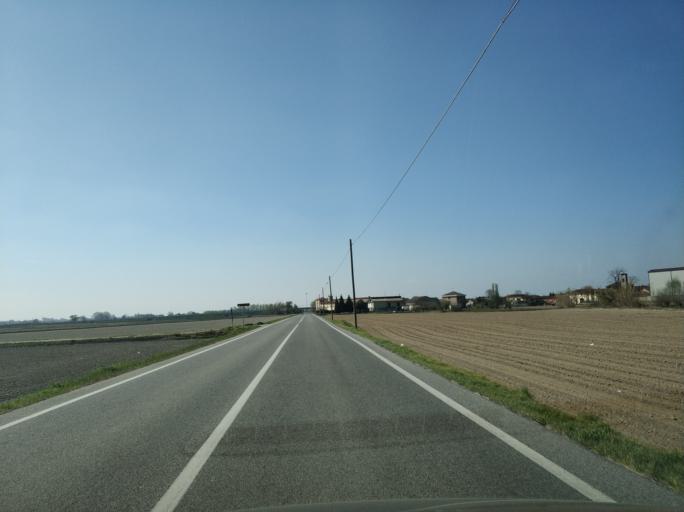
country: IT
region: Piedmont
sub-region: Provincia di Novara
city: Vinzaglio
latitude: 45.3210
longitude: 8.4816
